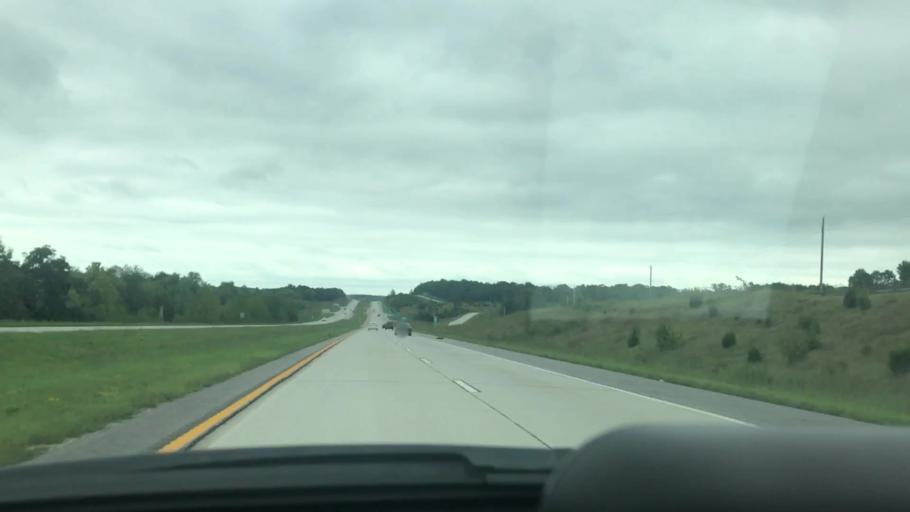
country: US
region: Missouri
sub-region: Greene County
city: Fair Grove
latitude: 37.5108
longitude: -93.1388
